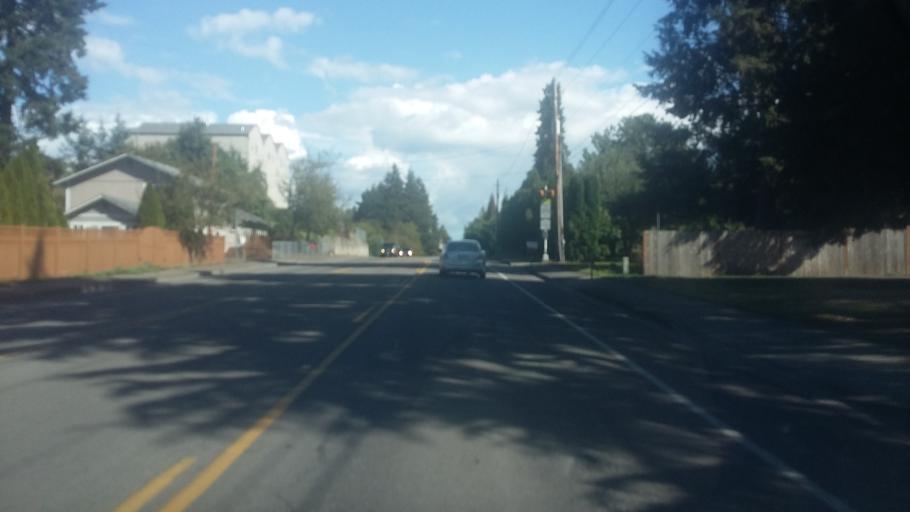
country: US
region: Washington
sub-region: Clark County
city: Salmon Creek
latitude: 45.6931
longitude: -122.6435
